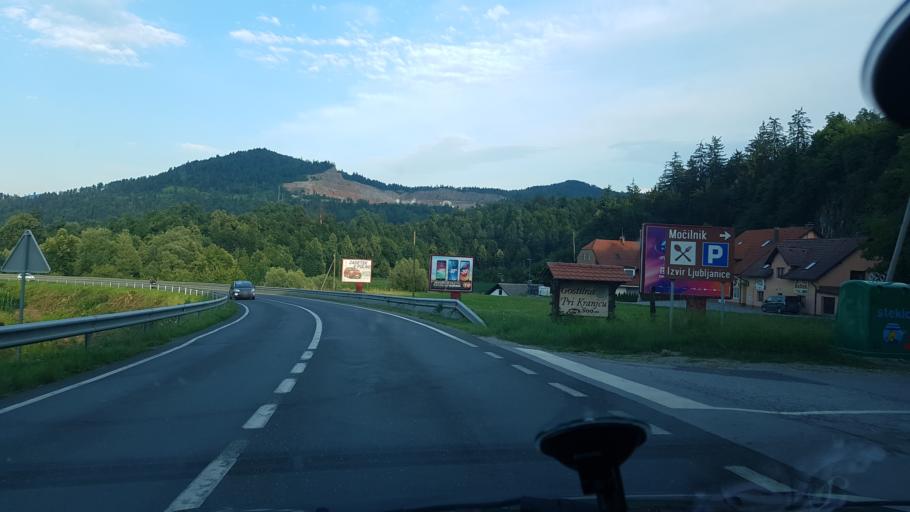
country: SI
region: Vrhnika
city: Vrhnika
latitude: 45.9585
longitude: 14.2897
